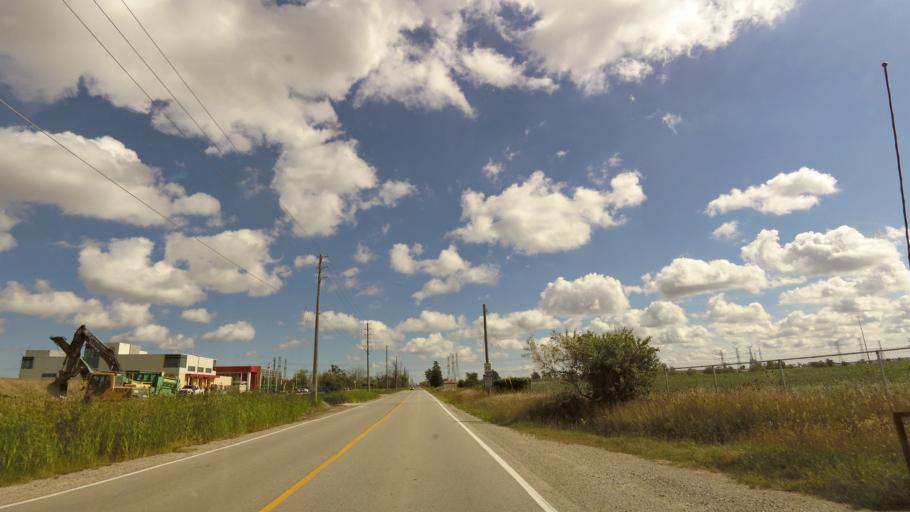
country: CA
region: Ontario
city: Brampton
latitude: 43.5879
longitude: -79.8054
